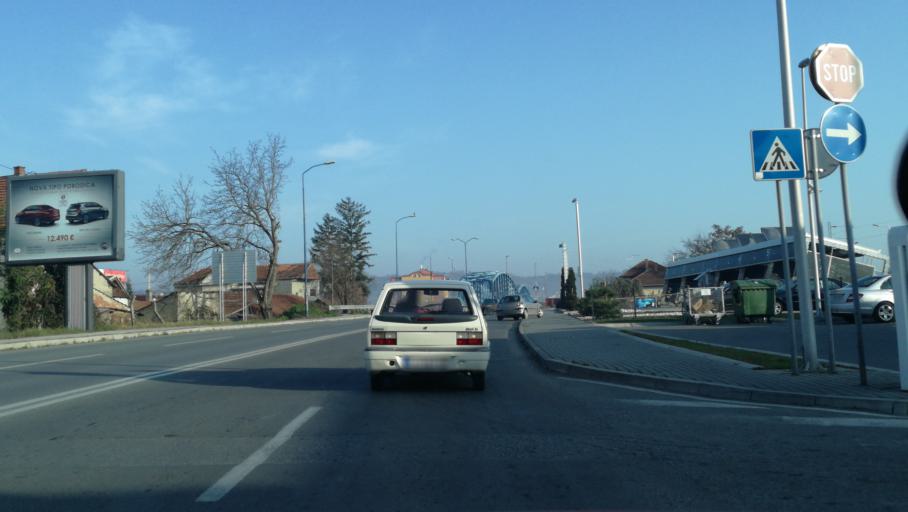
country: RS
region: Central Serbia
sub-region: Moravicki Okrug
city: Cacak
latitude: 43.8959
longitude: 20.3527
